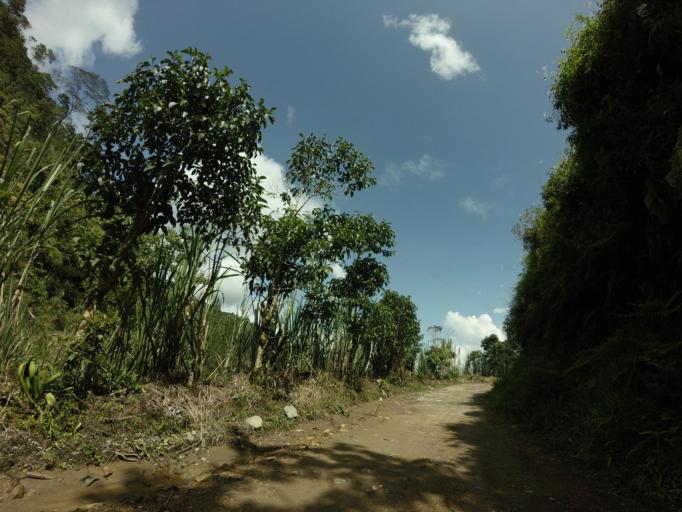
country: CO
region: Caldas
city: Pensilvania
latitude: 5.4715
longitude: -75.1858
